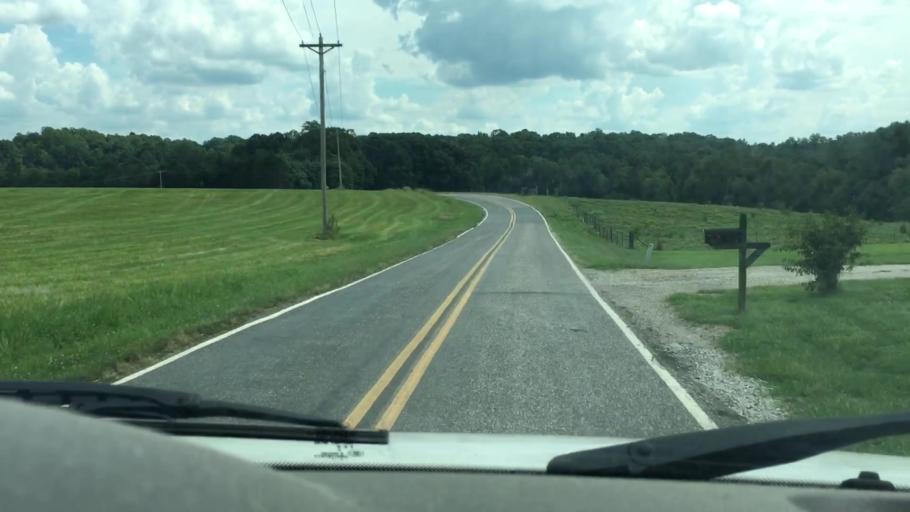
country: US
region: North Carolina
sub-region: Iredell County
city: Mooresville
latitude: 35.6631
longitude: -80.8164
